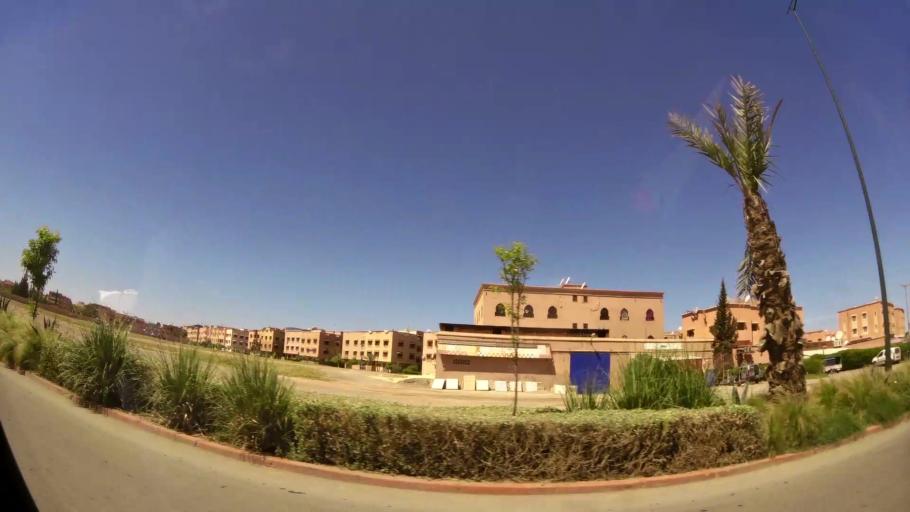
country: MA
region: Marrakech-Tensift-Al Haouz
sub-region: Marrakech
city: Marrakesh
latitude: 31.6592
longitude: -7.9845
